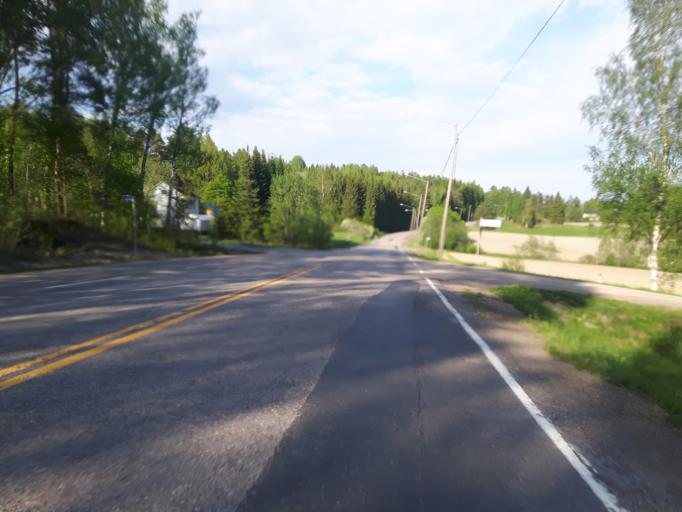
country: FI
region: Uusimaa
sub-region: Loviisa
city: Perna
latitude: 60.4953
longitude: 25.9064
